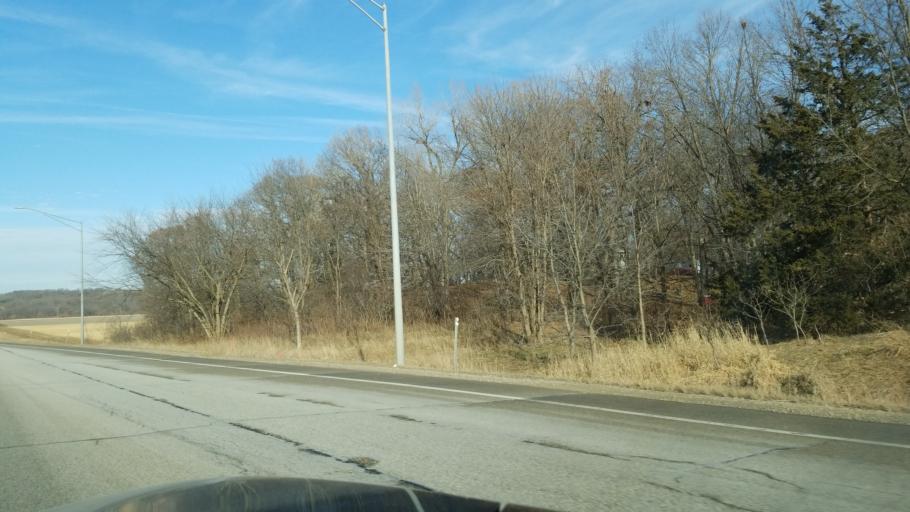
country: US
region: Iowa
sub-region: Linn County
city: Ely
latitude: 41.9297
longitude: -91.5426
